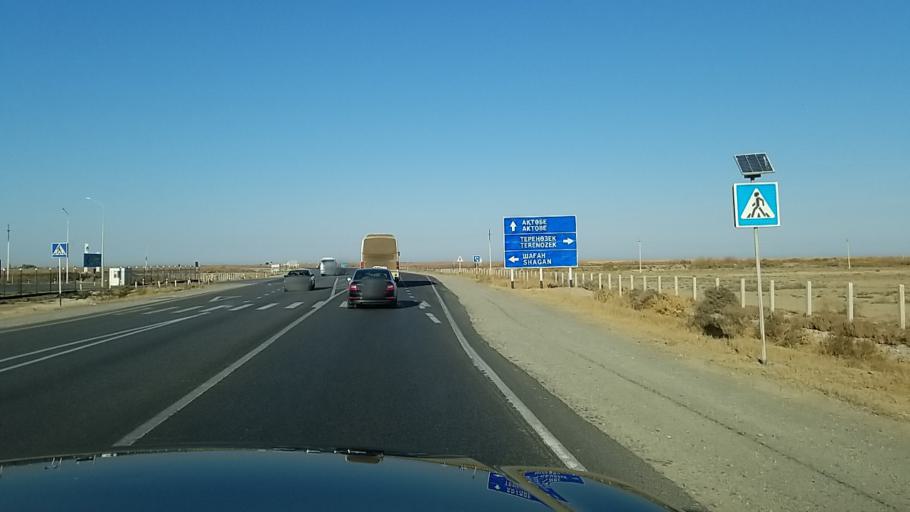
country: KZ
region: Qyzylorda
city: Terenozek
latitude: 44.9054
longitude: 64.9737
